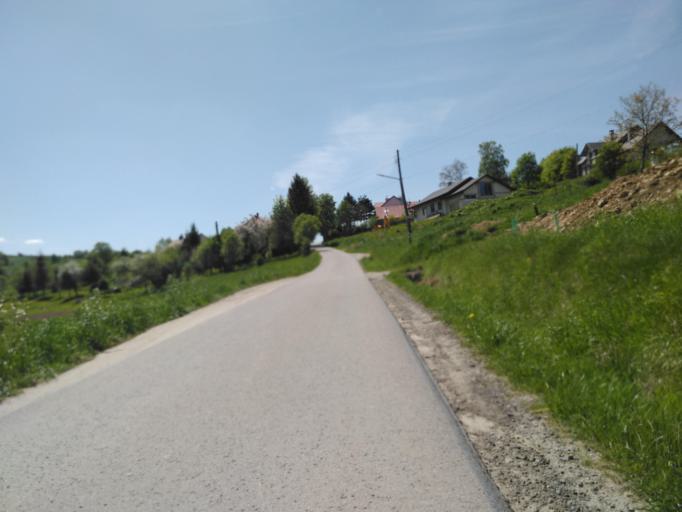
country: PL
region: Subcarpathian Voivodeship
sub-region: Powiat krosnienski
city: Iwonicz-Zdroj
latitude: 49.5463
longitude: 21.7780
